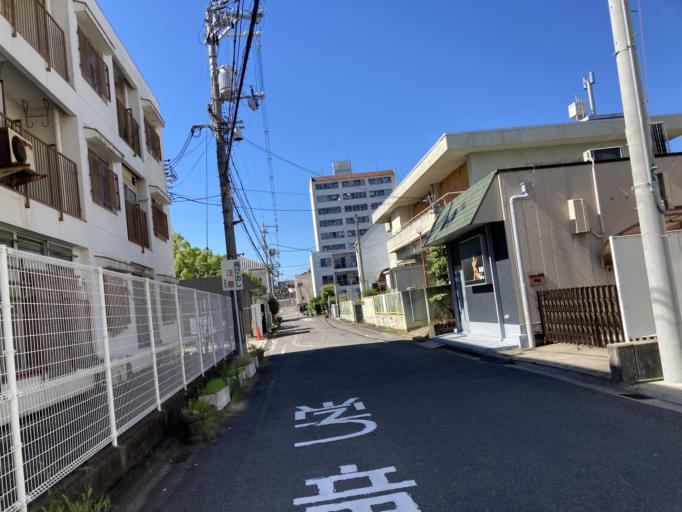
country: JP
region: Nara
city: Nara-shi
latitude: 34.6827
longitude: 135.8223
